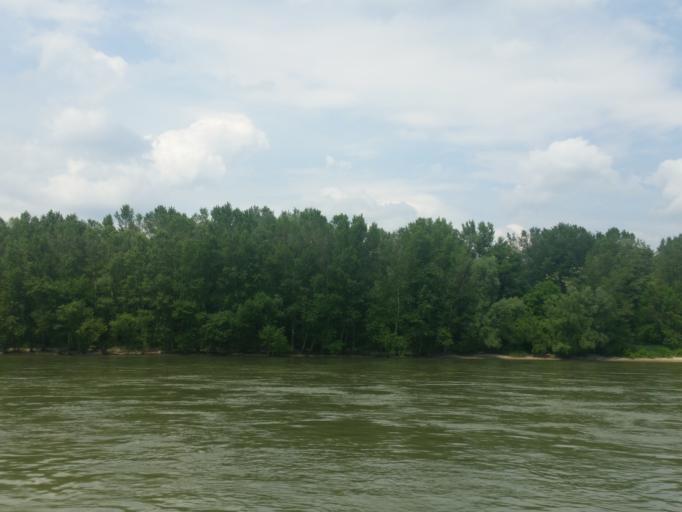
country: AT
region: Lower Austria
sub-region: Politischer Bezirk Bruck an der Leitha
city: Wolfsthal
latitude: 48.1401
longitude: 17.0393
